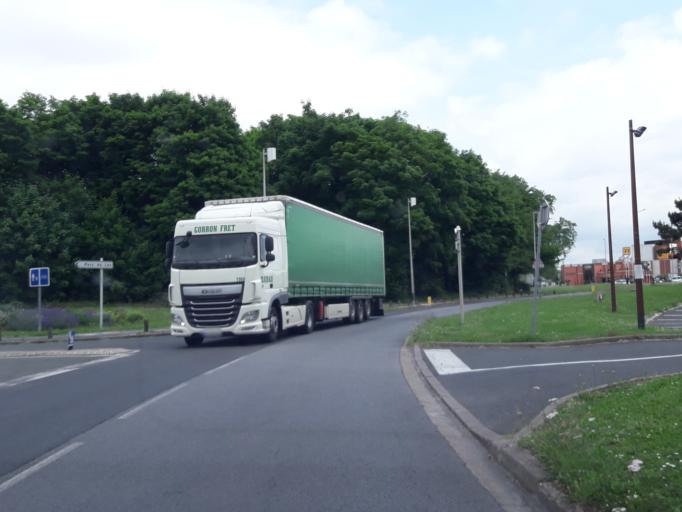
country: FR
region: Ile-de-France
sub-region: Departement de l'Essonne
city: Lisses
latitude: 48.6138
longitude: 2.4221
